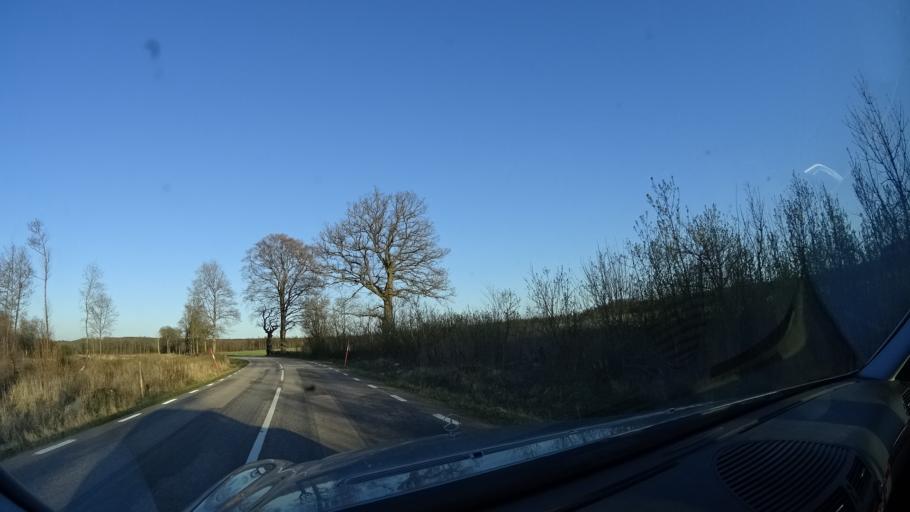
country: SE
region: Skane
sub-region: Svalovs Kommun
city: Kagerod
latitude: 55.9782
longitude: 13.1467
